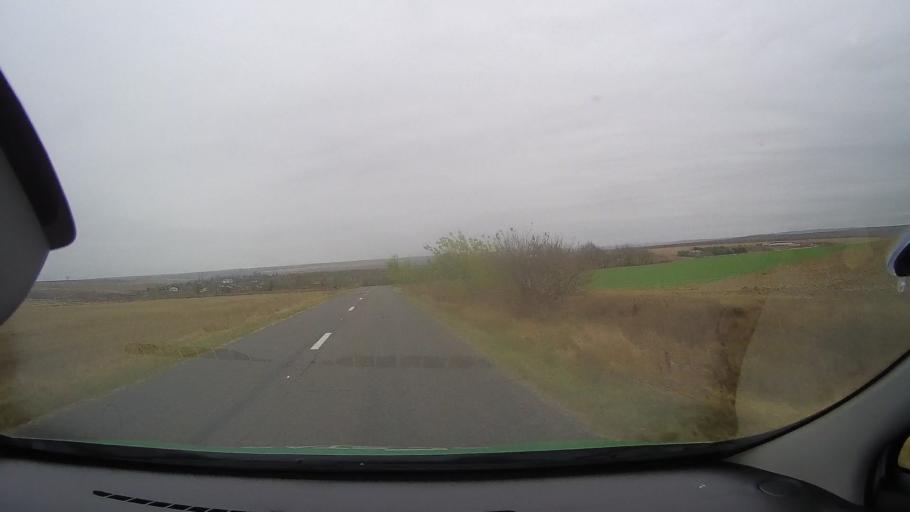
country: RO
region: Constanta
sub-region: Comuna Vulturu
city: Vulturu
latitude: 44.6952
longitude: 28.2420
